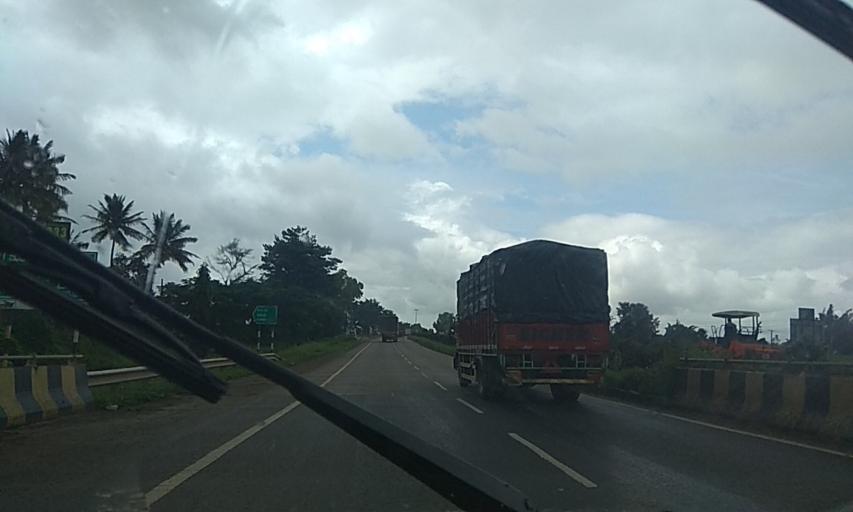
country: IN
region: Karnataka
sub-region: Belgaum
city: Sankeshwar
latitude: 16.2947
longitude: 74.4380
